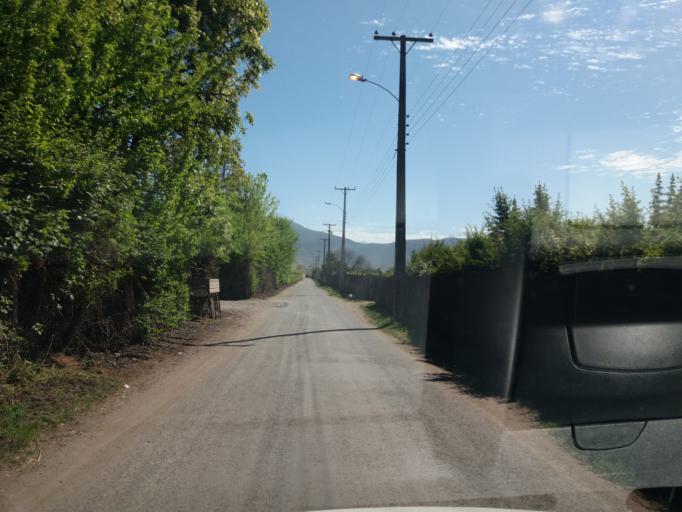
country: CL
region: Valparaiso
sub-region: Provincia de Quillota
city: Quillota
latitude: -32.8662
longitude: -71.2130
